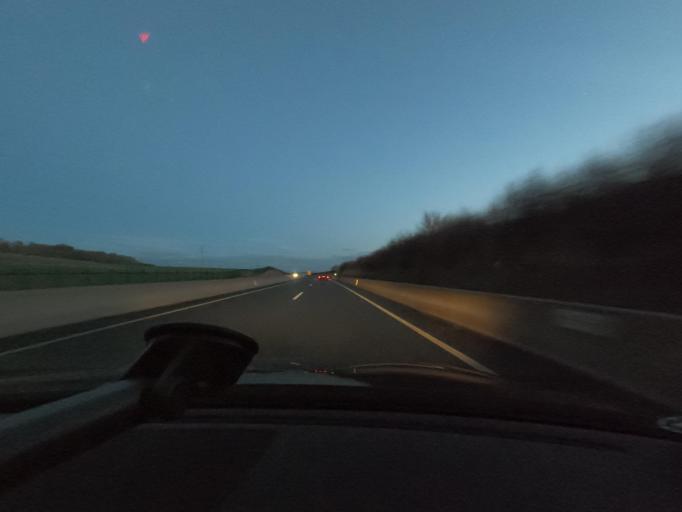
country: DE
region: Lower Saxony
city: Bad Lauterberg im Harz
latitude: 51.5929
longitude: 10.4931
